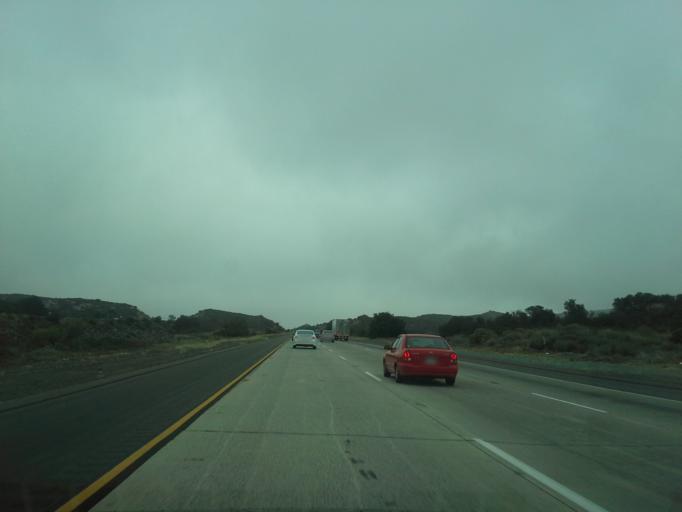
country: US
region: California
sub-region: San Diego County
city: Descanso
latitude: 32.8214
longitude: -116.5940
